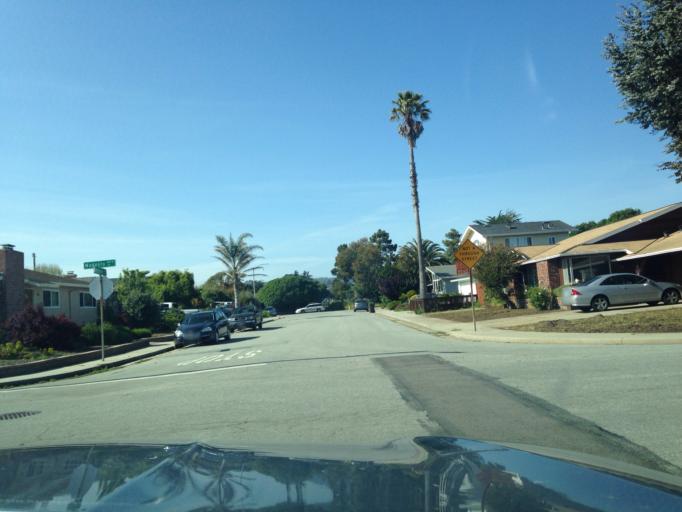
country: US
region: California
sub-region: Santa Cruz County
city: Santa Cruz
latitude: 36.9515
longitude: -122.0489
